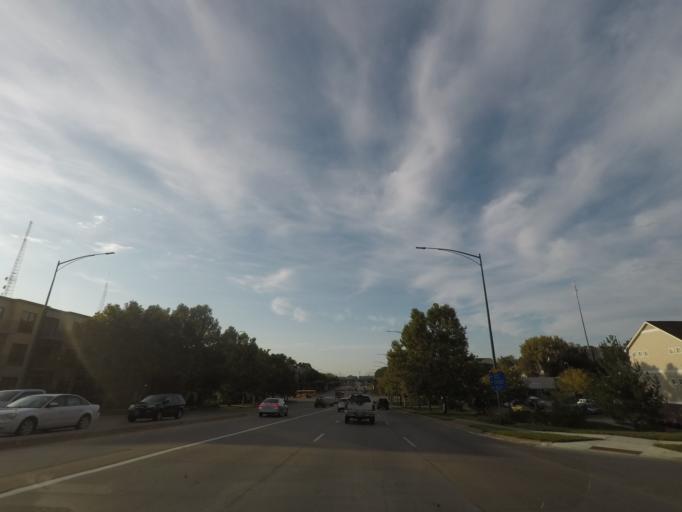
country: US
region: Iowa
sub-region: Polk County
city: Des Moines
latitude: 41.5872
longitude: -93.6449
